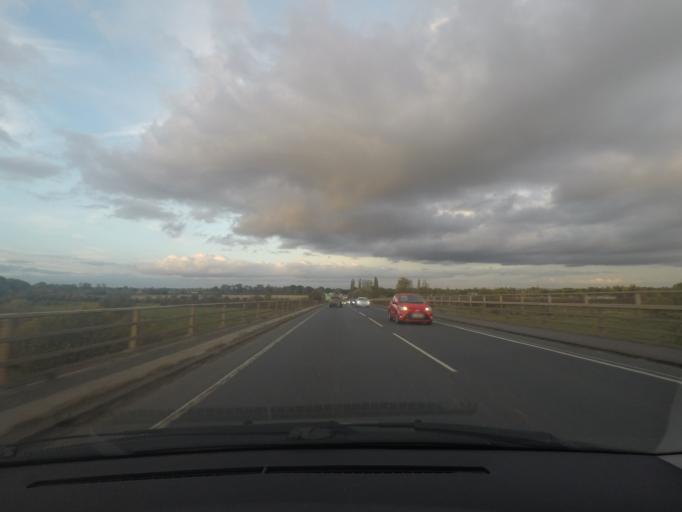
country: GB
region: England
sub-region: City of York
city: Skelton
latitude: 53.9831
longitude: -1.1302
